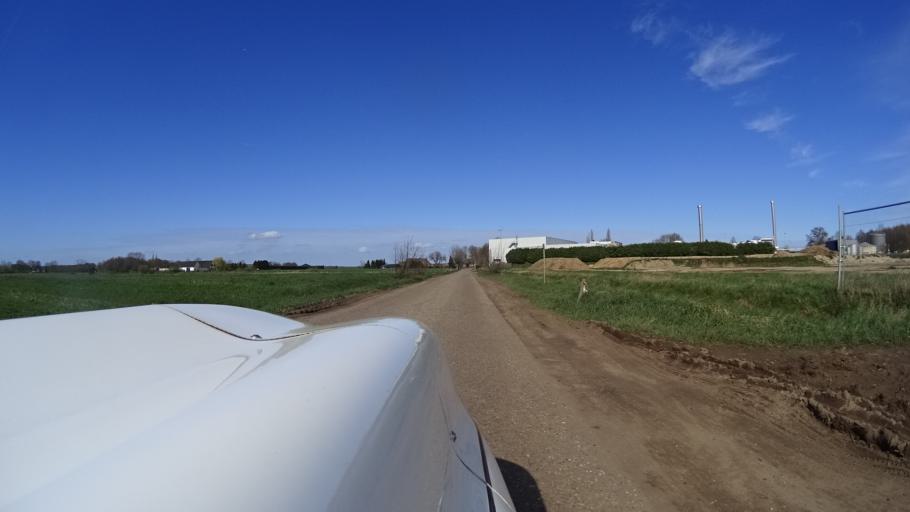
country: NL
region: Limburg
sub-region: Gemeente Bergen
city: Wellerlooi
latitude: 51.5052
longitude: 6.1497
